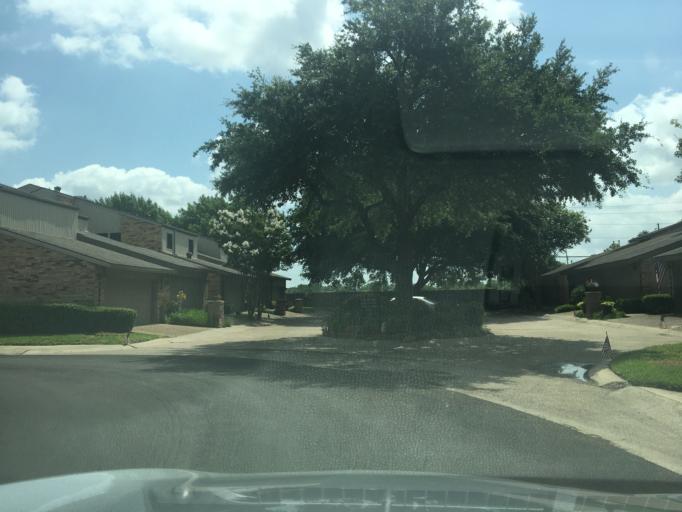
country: US
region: Texas
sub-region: Dallas County
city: Addison
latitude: 32.9187
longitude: -96.8133
